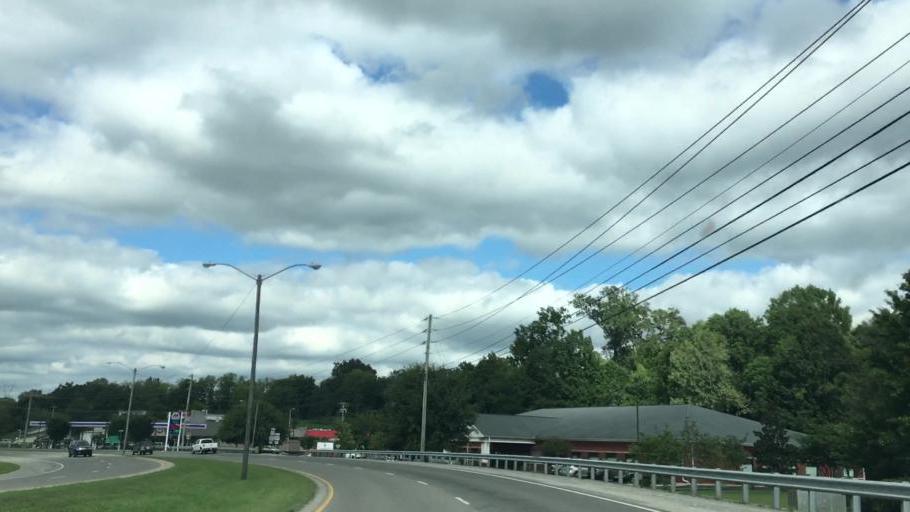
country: US
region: Tennessee
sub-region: Maury County
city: Columbia
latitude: 35.6154
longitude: -87.0653
